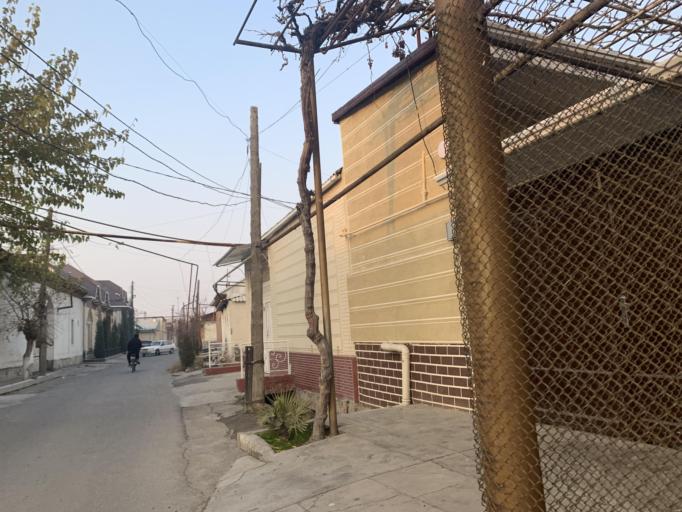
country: UZ
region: Fergana
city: Qo`qon
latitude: 40.5328
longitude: 70.9308
